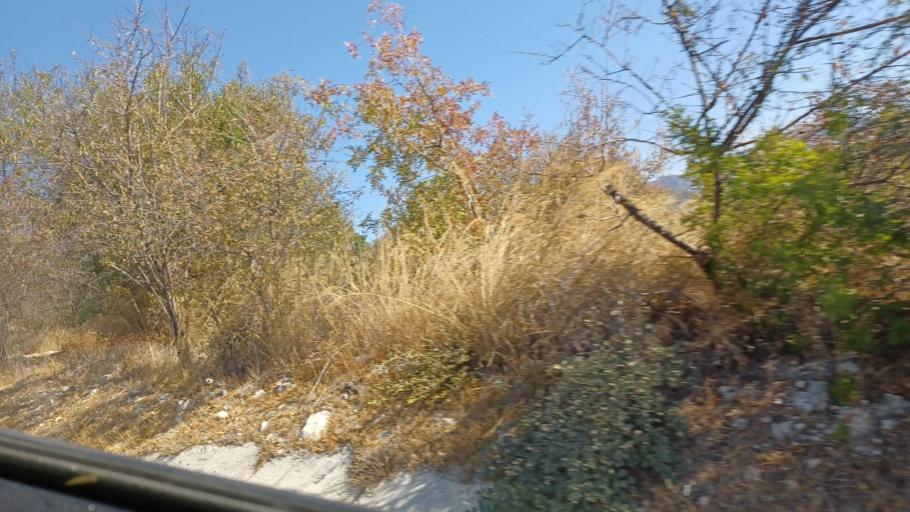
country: CY
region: Pafos
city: Mesogi
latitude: 34.9239
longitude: 32.5654
